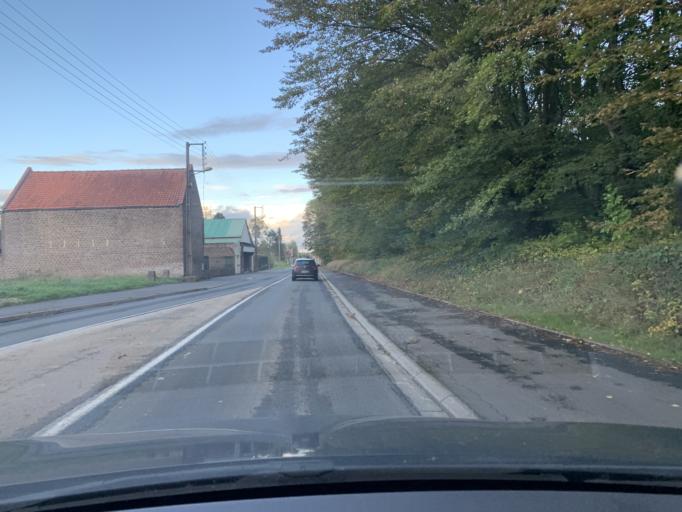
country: FR
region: Nord-Pas-de-Calais
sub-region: Departement du Nord
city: Proville
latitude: 50.1624
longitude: 3.2138
